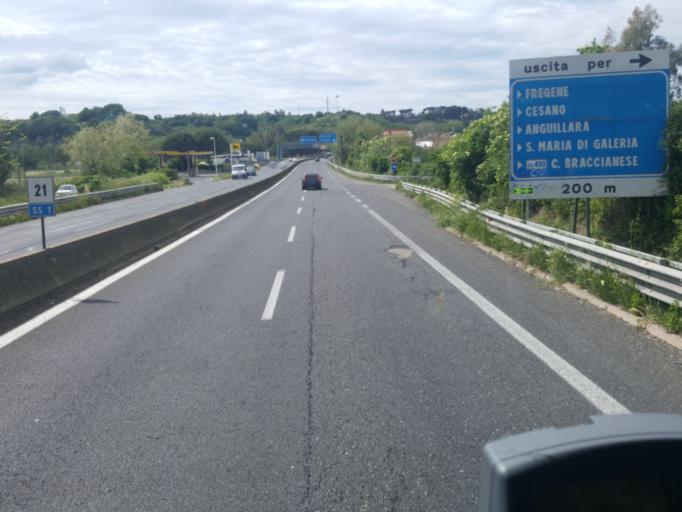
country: IT
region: Latium
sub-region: Citta metropolitana di Roma Capitale
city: Ara Nova
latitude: 41.9058
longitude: 12.2681
